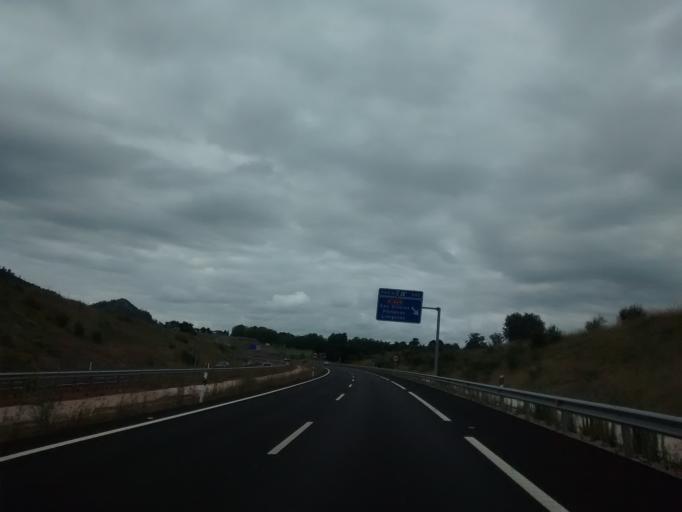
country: ES
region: Cantabria
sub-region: Provincia de Cantabria
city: Lierganes
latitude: 43.3586
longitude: -3.7634
